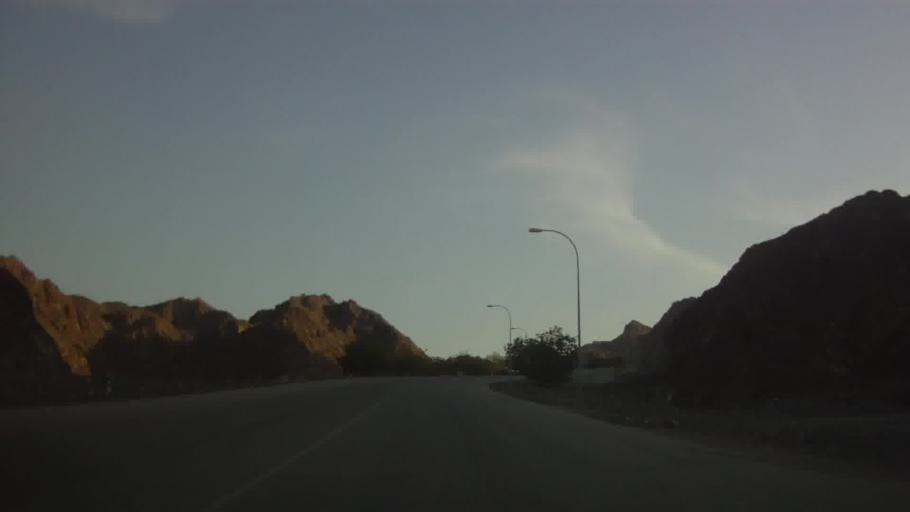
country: OM
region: Muhafazat Masqat
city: Muscat
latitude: 23.5919
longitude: 58.6030
